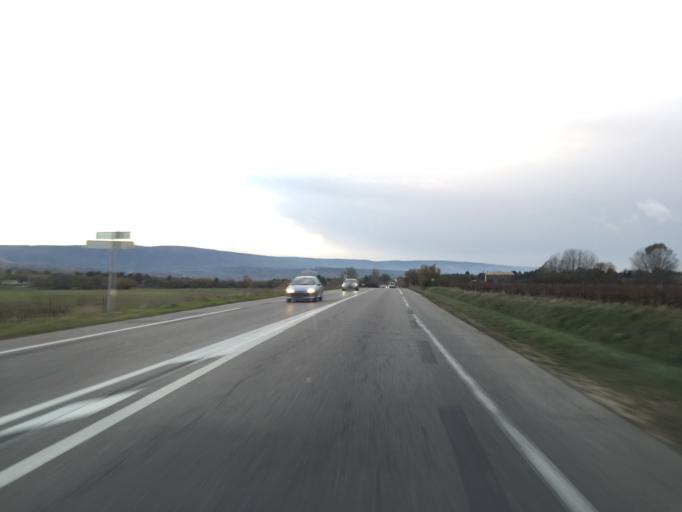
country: FR
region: Provence-Alpes-Cote d'Azur
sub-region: Departement du Vaucluse
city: Gargas
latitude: 43.8749
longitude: 5.3292
